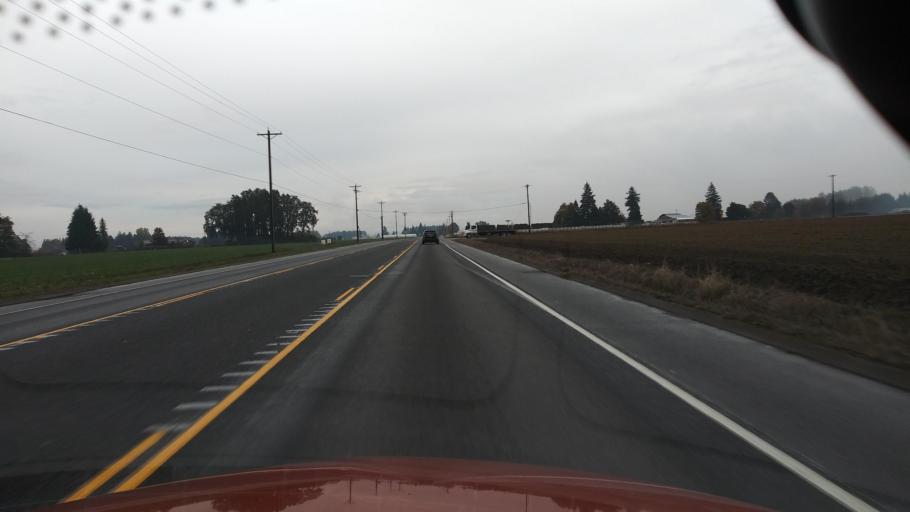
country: US
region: Oregon
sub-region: Washington County
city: Cornelius
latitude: 45.5608
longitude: -123.0563
